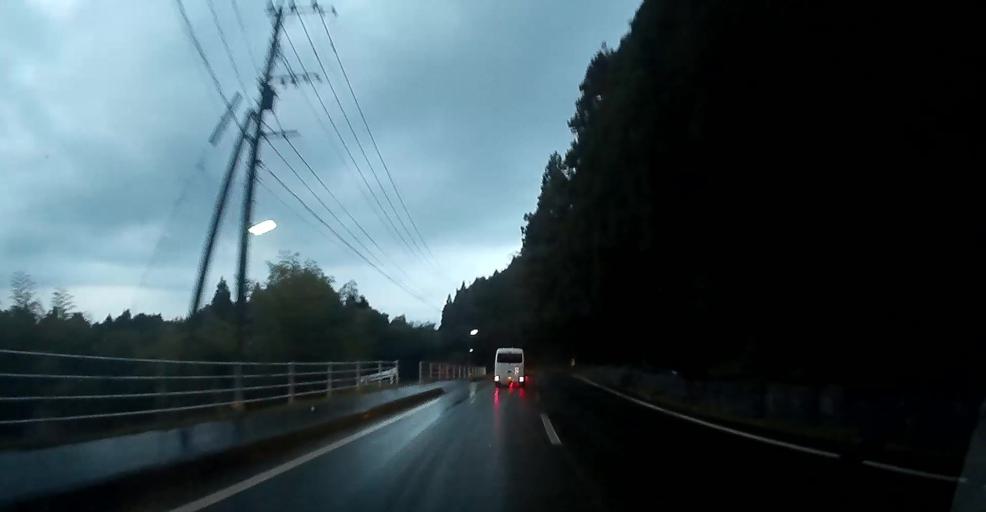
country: JP
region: Kumamoto
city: Ozu
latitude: 32.8352
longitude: 130.9148
